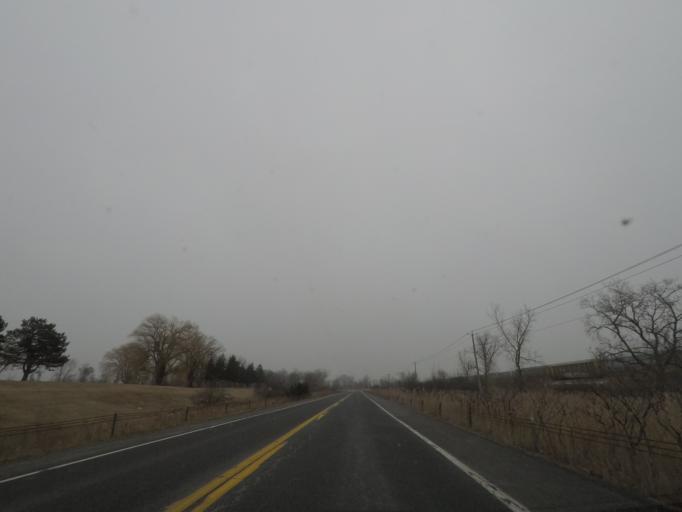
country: US
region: New York
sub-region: Albany County
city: Delmar
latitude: 42.5703
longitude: -73.8553
